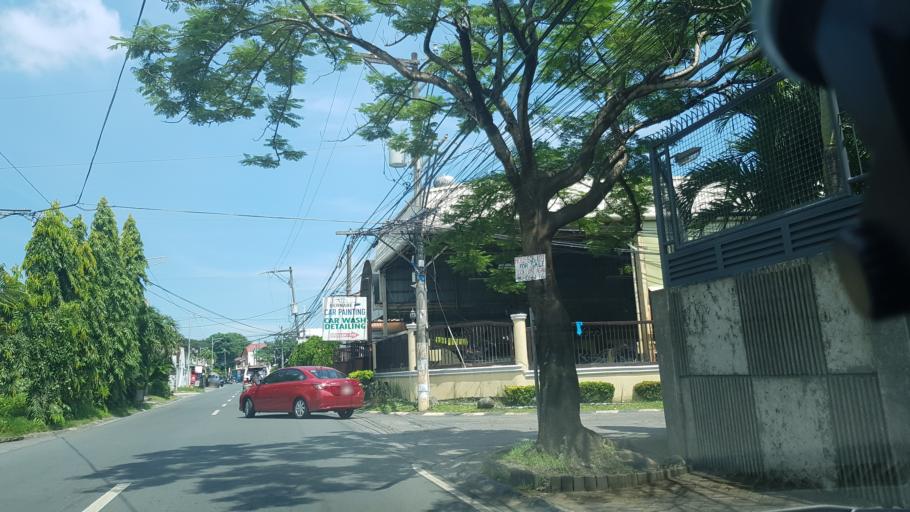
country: PH
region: Calabarzon
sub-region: Province of Rizal
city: Las Pinas
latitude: 14.4341
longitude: 120.9938
